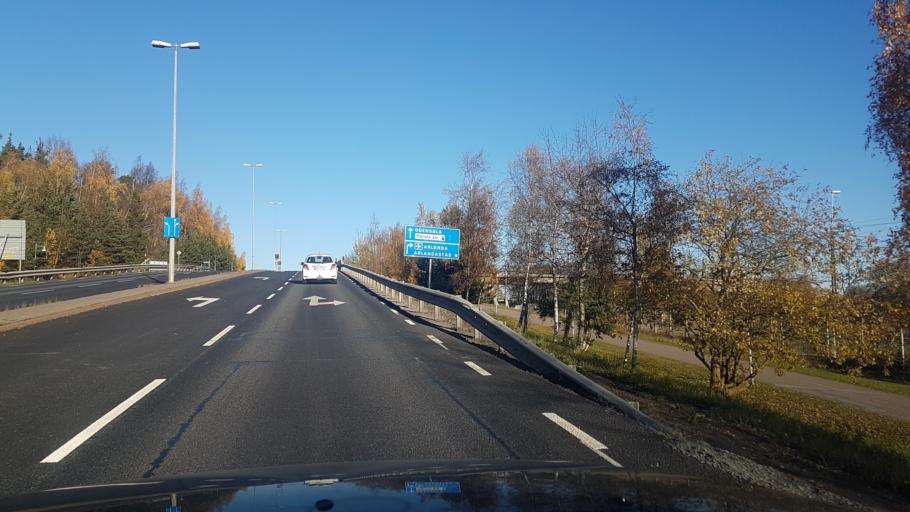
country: SE
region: Stockholm
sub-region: Sigtuna Kommun
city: Marsta
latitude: 59.6223
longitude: 17.8596
